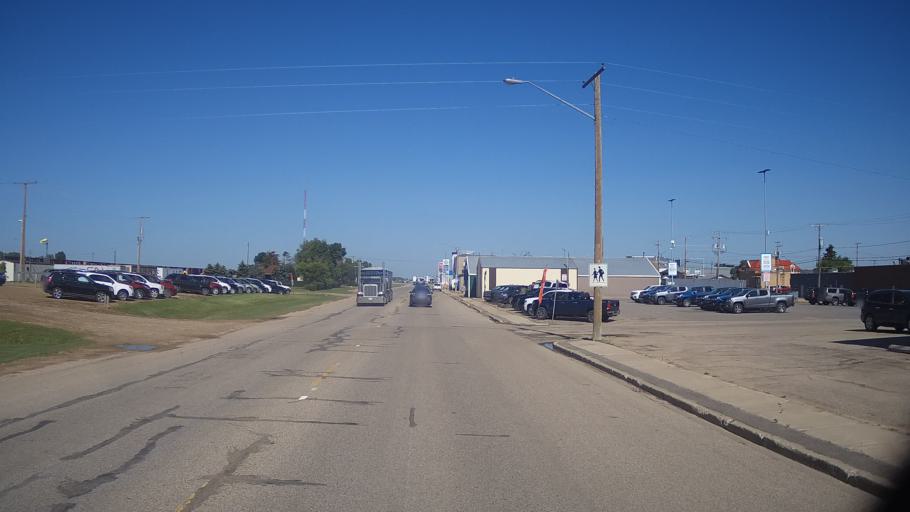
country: CA
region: Saskatchewan
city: Watrous
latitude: 51.6711
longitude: -105.4663
